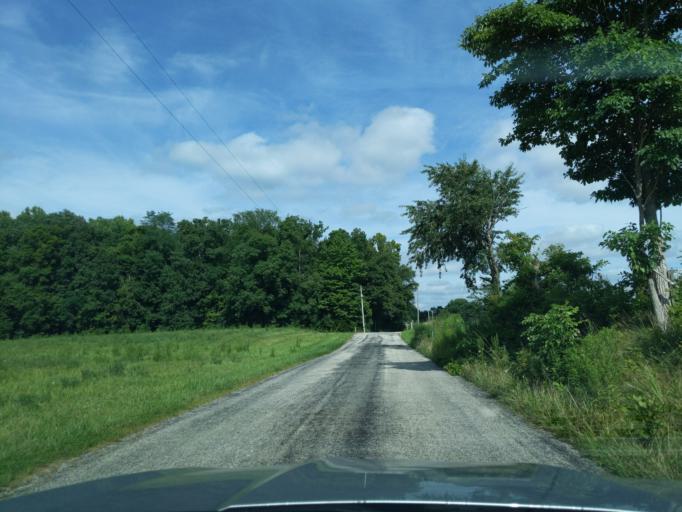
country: US
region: Indiana
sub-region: Decatur County
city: Greensburg
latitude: 39.2350
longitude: -85.4033
